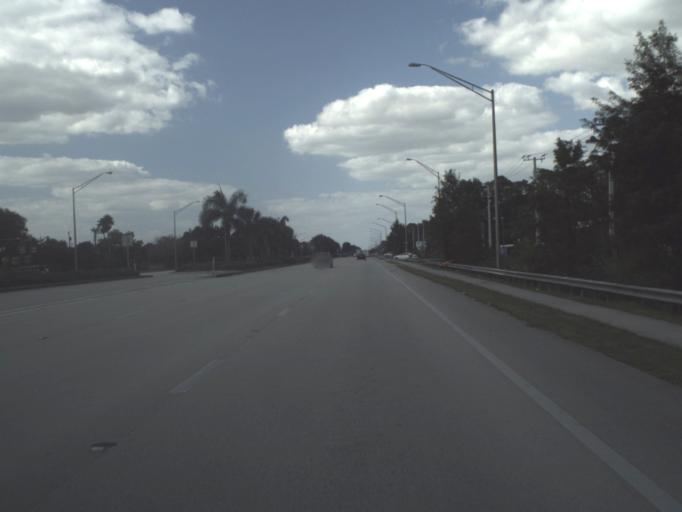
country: US
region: Florida
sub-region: Collier County
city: Naples Manor
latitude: 26.0875
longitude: -81.7298
